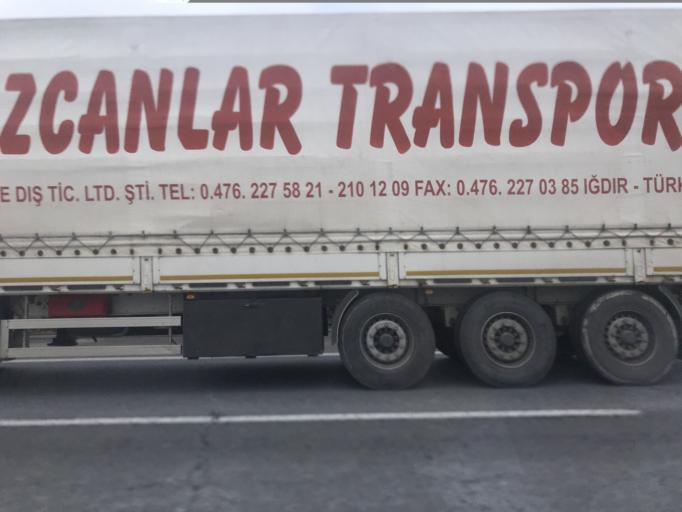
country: TR
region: Bolu
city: Bolu
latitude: 40.7736
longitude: 31.7298
